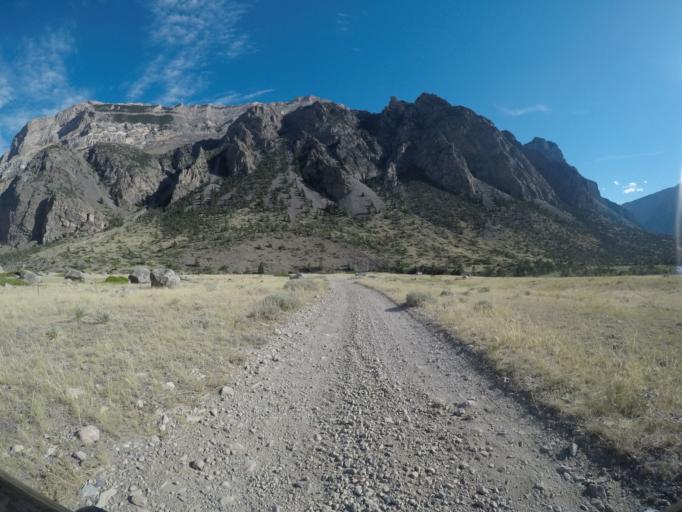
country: US
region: Montana
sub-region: Carbon County
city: Red Lodge
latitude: 44.8436
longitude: -109.3169
